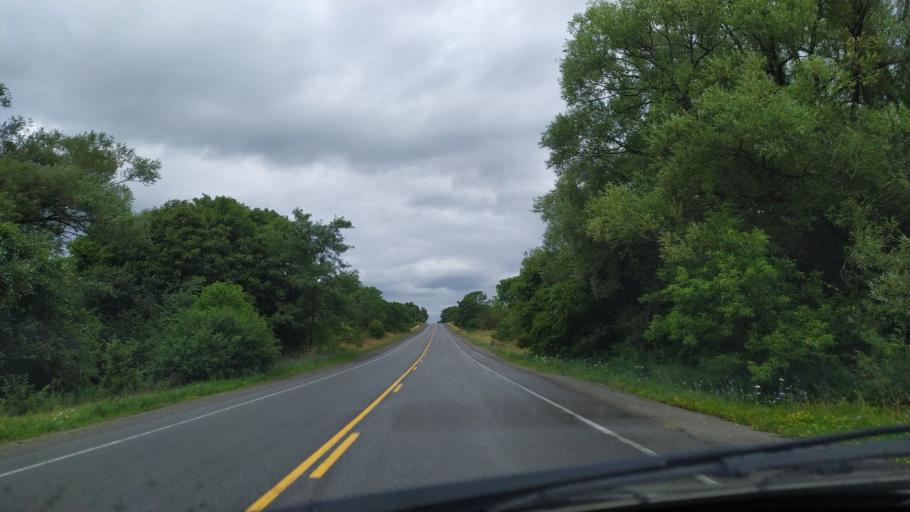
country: CA
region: Ontario
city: Quinte West
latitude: 43.9673
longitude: -77.5014
